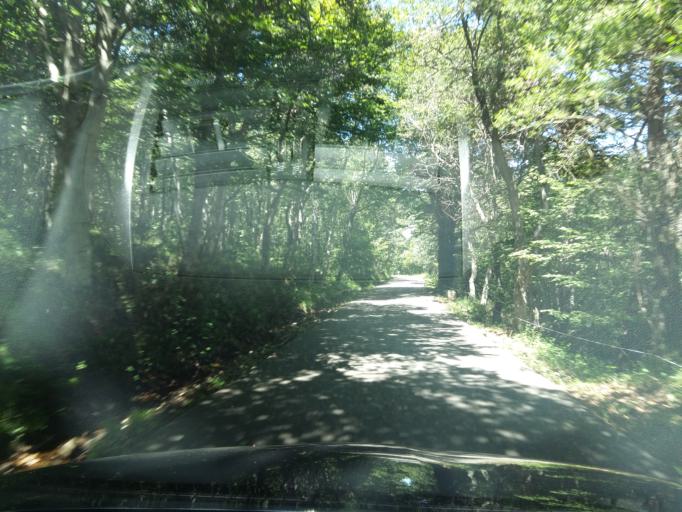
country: ES
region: Castille and Leon
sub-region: Provincia de Soria
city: Vozmediano
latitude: 41.8040
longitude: -1.8128
